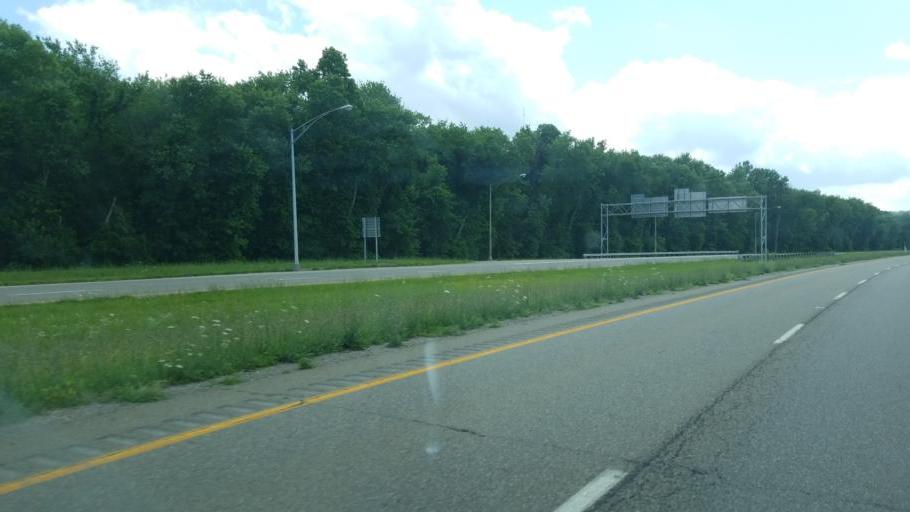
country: US
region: Ohio
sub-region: Tuscarawas County
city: Dover
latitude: 40.4898
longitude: -81.4788
